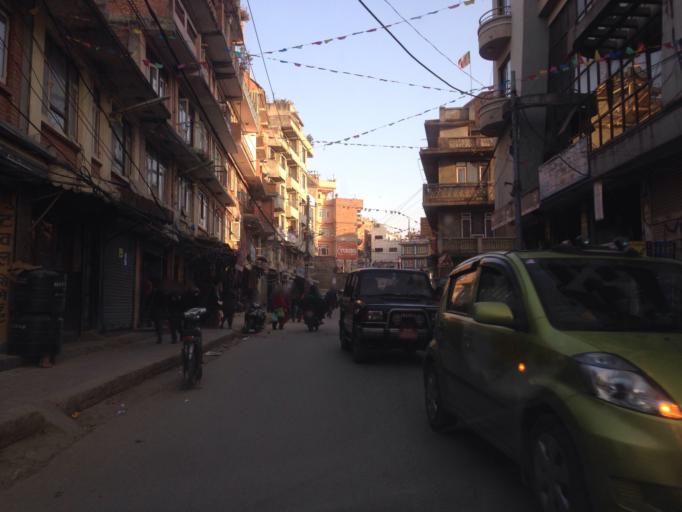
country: NP
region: Central Region
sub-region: Bagmati Zone
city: Kathmandu
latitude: 27.7137
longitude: 85.3032
